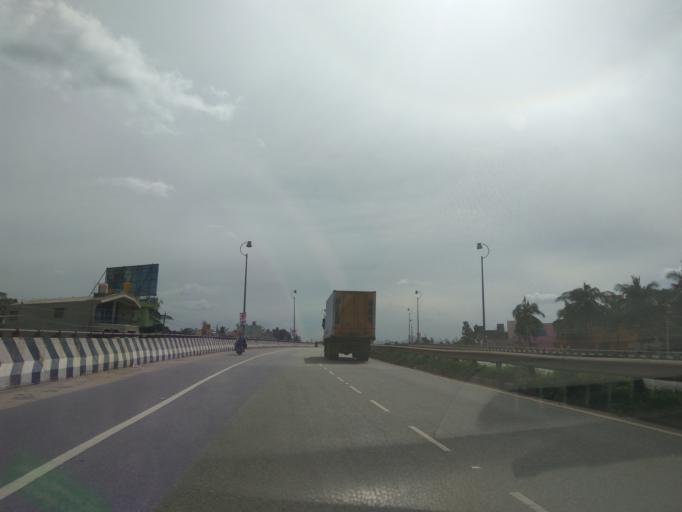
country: IN
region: Karnataka
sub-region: Bangalore Rural
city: Dasarahalli
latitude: 13.1325
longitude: 77.9284
